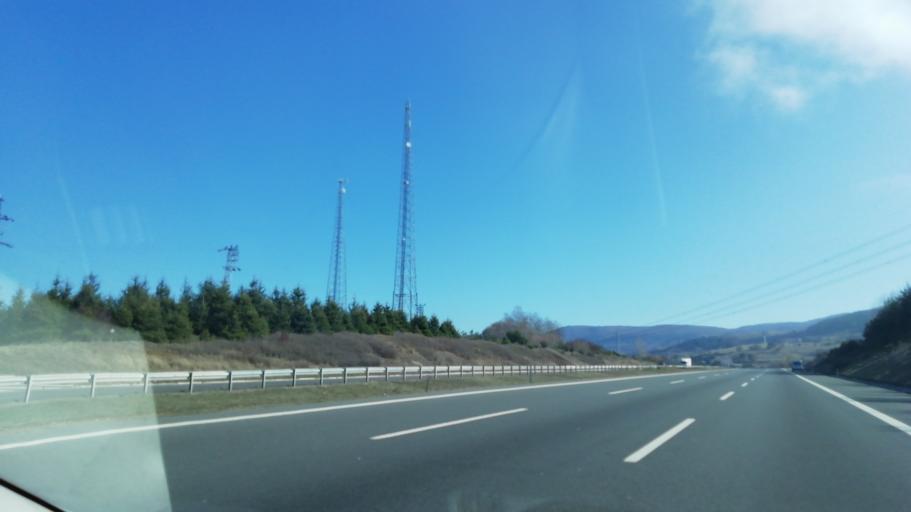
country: TR
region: Bolu
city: Yenicaga
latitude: 40.7523
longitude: 31.9262
